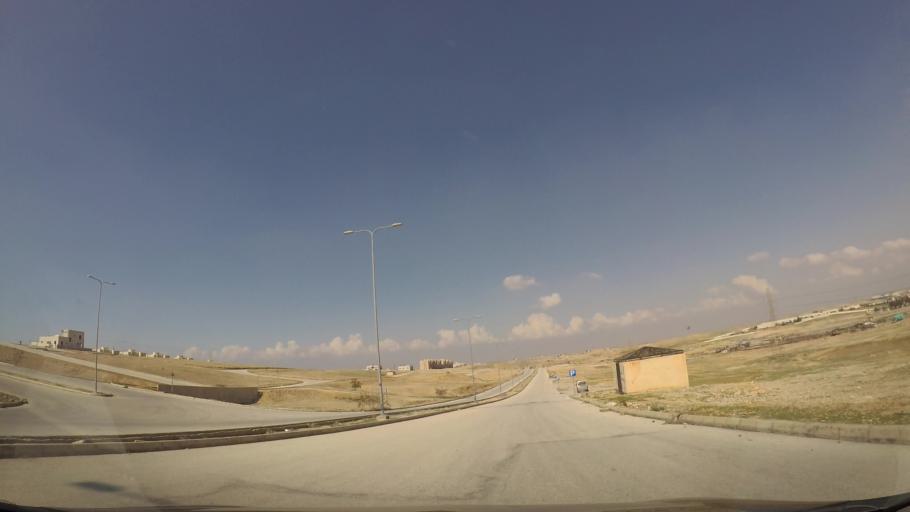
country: JO
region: Zarqa
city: Zarqa
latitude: 32.0502
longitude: 36.1226
